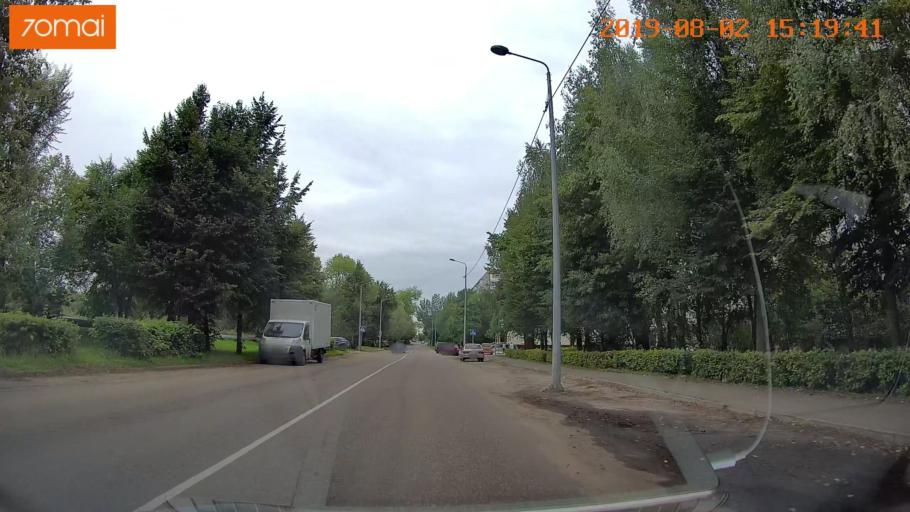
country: RU
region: Moskovskaya
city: Voskresensk
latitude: 55.3119
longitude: 38.6443
